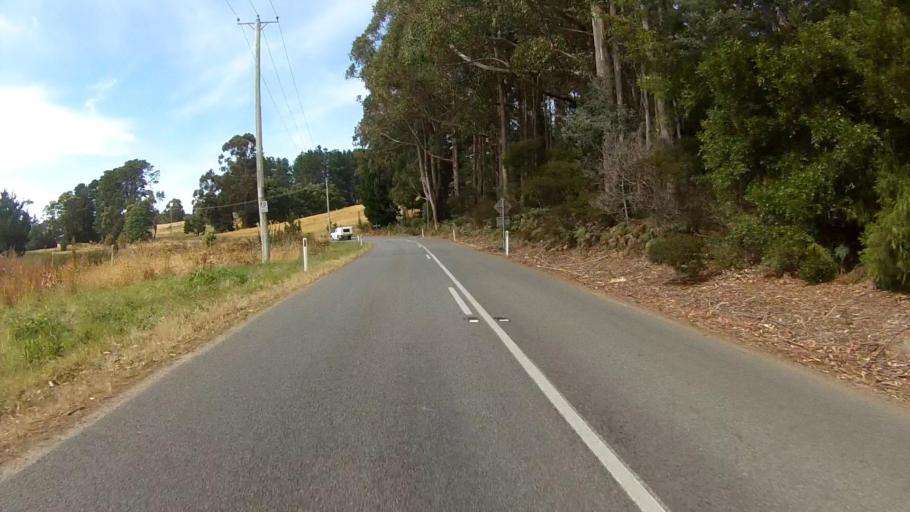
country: AU
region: Tasmania
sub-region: Kingborough
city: Kettering
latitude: -43.1927
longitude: 147.2476
